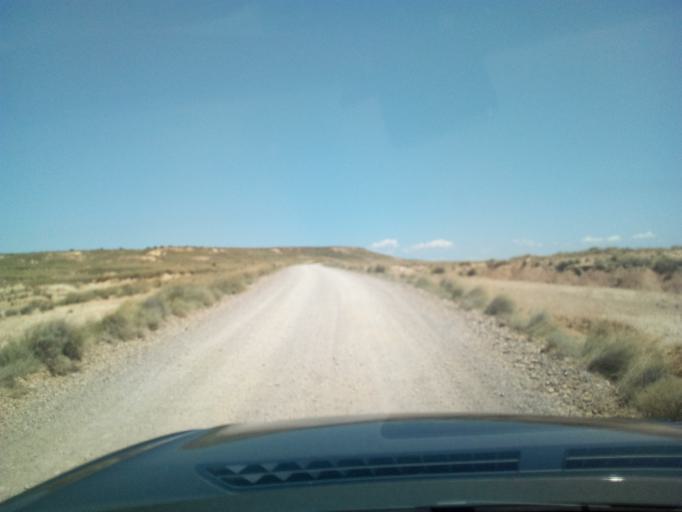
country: ES
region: Navarre
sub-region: Provincia de Navarra
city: Fustinana
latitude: 42.1691
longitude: -1.4238
